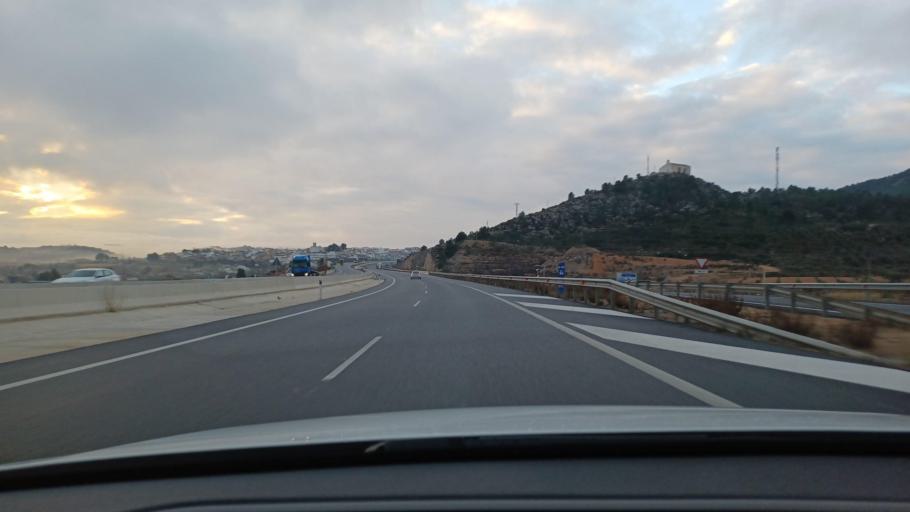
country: ES
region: Valencia
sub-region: Provincia de Valencia
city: La Font de la Figuera
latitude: 38.8177
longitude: -0.8898
